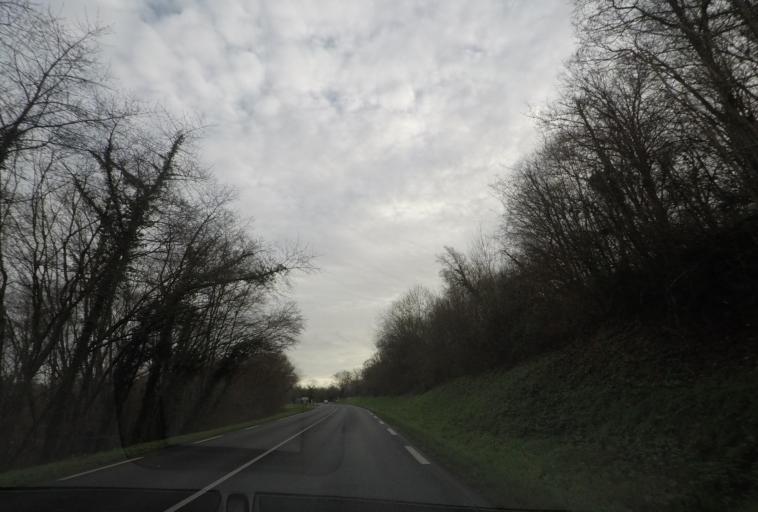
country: FR
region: Centre
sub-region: Departement du Loir-et-Cher
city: Sarge-sur-Braye
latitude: 47.9092
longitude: 0.8552
